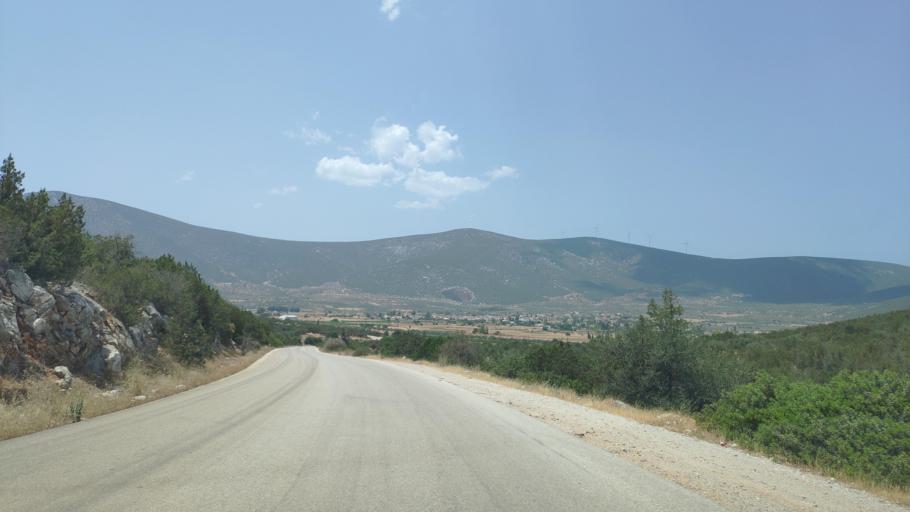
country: GR
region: Peloponnese
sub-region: Nomos Argolidos
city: Didyma
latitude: 37.4457
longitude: 23.1828
